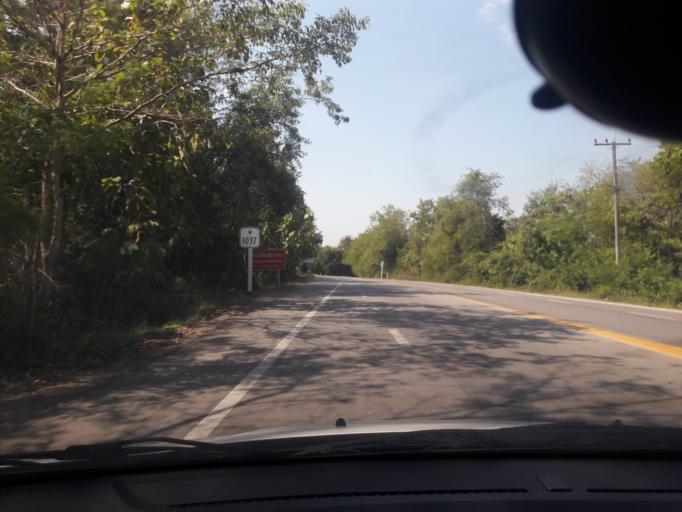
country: TH
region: Lampang
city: Mae Tha
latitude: 18.1877
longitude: 99.5467
